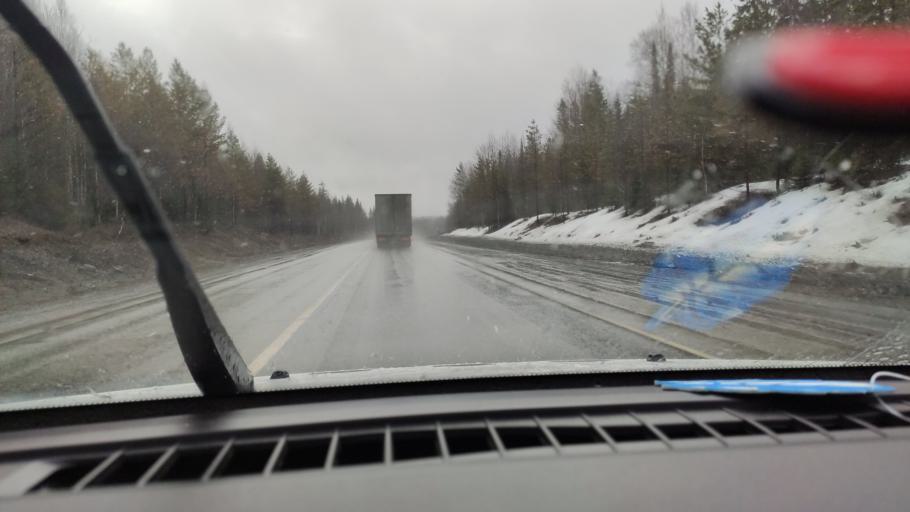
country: RU
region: Sverdlovsk
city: Atig
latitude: 56.8226
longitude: 59.3306
